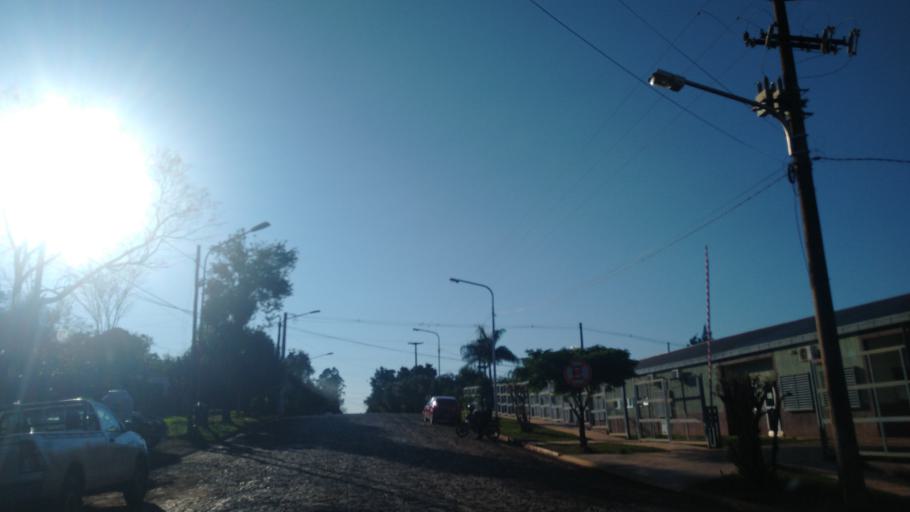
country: AR
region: Misiones
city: Puerto Libertad
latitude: -25.9715
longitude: -54.5567
